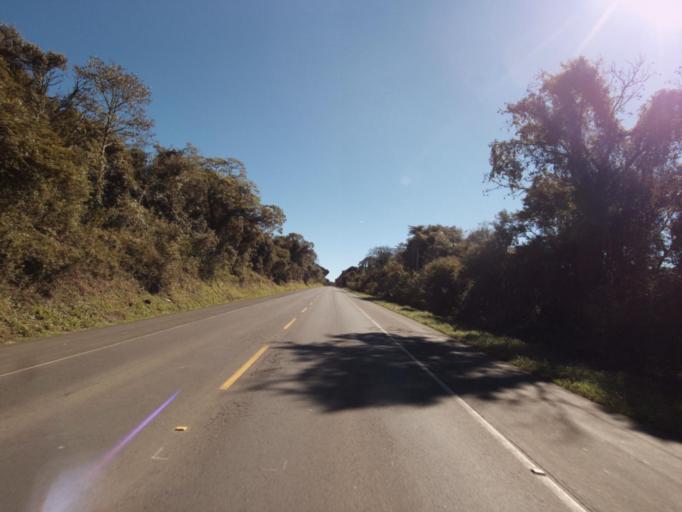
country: BR
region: Santa Catarina
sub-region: Joacaba
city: Joacaba
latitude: -27.1272
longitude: -51.6289
